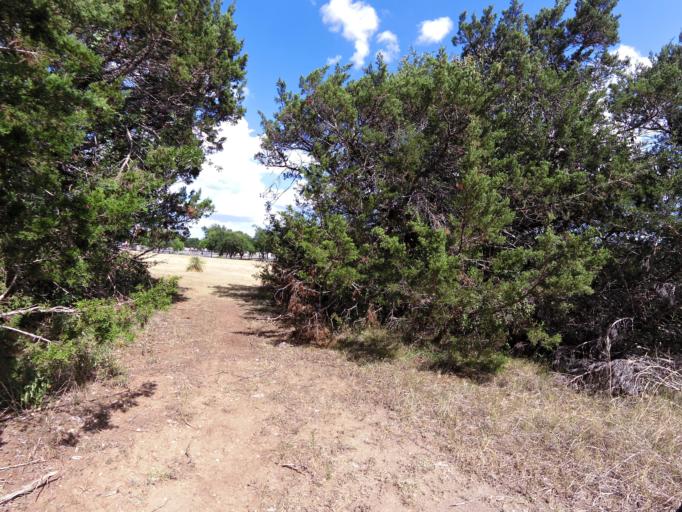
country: US
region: Texas
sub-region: Bexar County
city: Helotes
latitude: 29.5790
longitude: -98.6306
